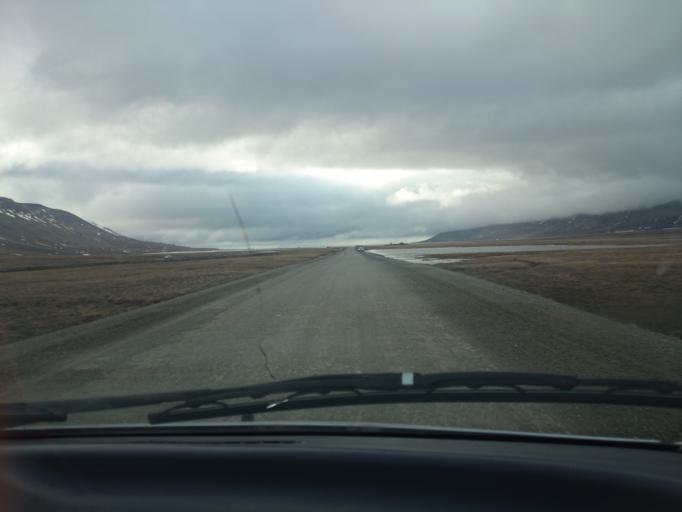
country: SJ
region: Svalbard
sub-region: Spitsbergen
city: Longyearbyen
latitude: 78.1936
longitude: 15.8584
